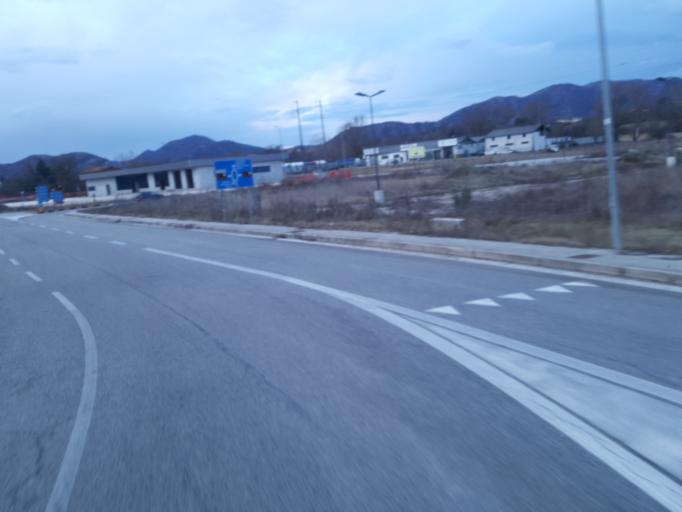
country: IT
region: Abruzzo
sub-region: Provincia dell' Aquila
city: Carsoli
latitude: 42.0813
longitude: 13.0583
